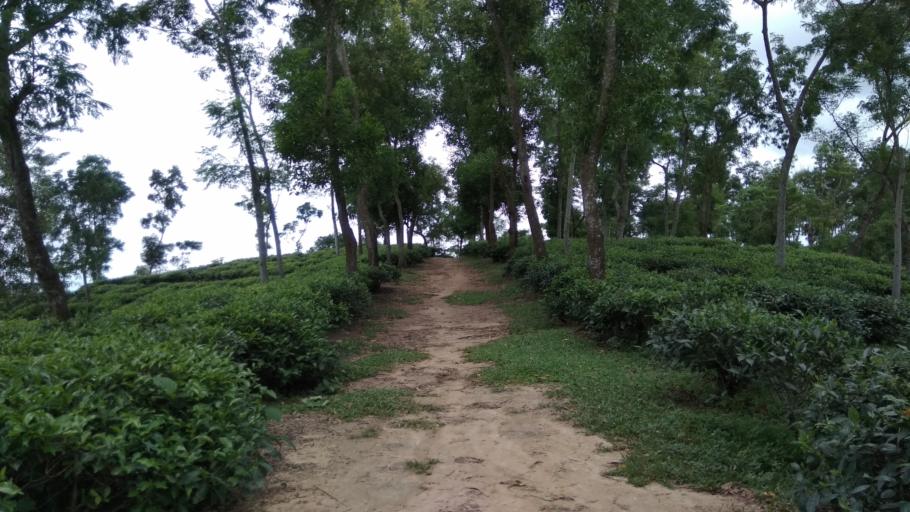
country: IN
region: Tripura
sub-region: Dhalai
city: Kamalpur
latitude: 24.2802
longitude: 91.8198
